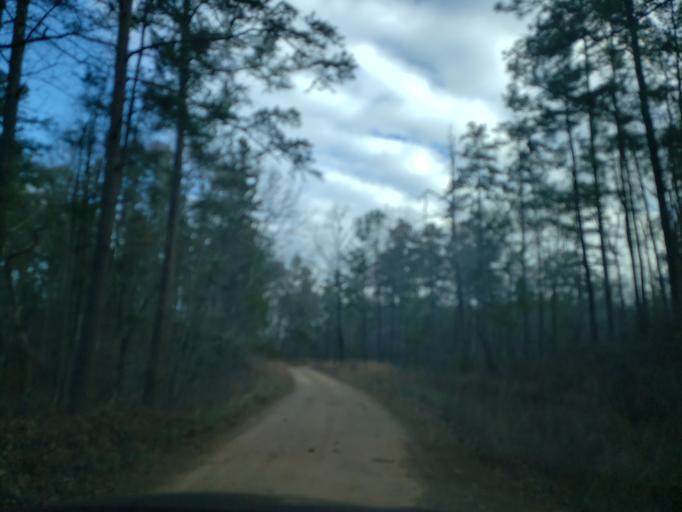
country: US
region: Alabama
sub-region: Cleburne County
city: Heflin
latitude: 33.7019
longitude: -85.6279
